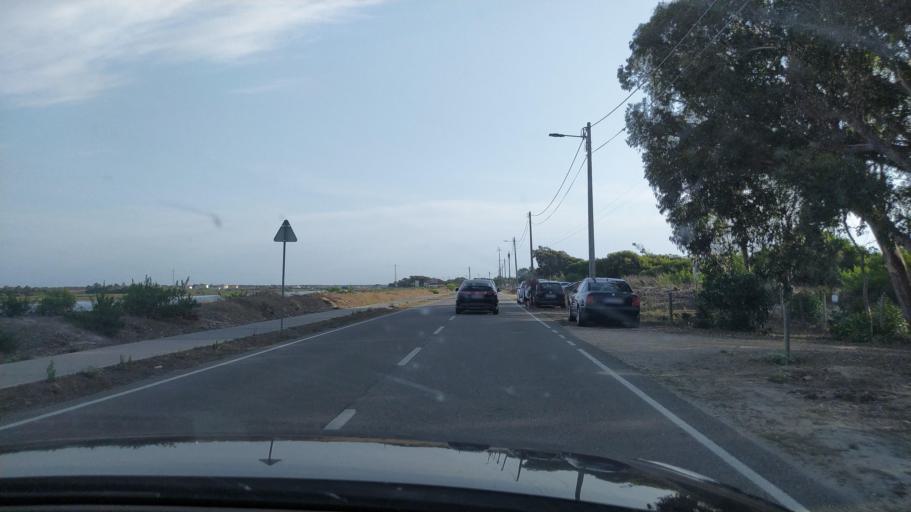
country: PT
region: Aveiro
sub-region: Ilhavo
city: Gafanha da Encarnacao
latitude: 40.5767
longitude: -8.7553
